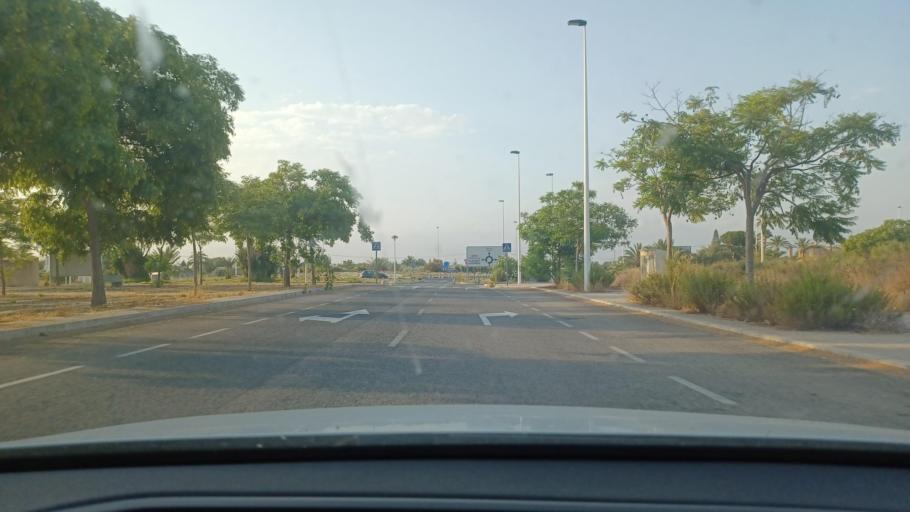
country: ES
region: Valencia
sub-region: Provincia de Alicante
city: Elche
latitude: 38.2855
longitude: -0.6239
